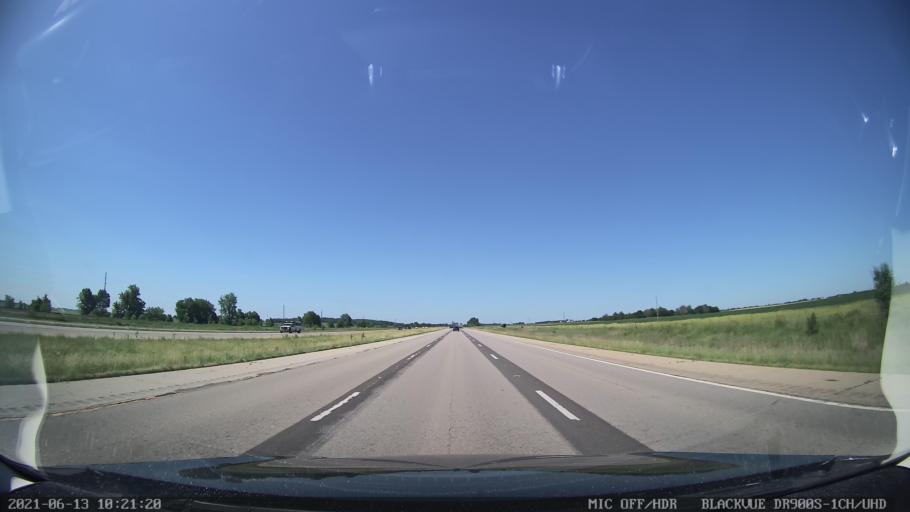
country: US
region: Illinois
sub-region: Logan County
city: Lincoln
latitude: 40.0540
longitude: -89.4567
